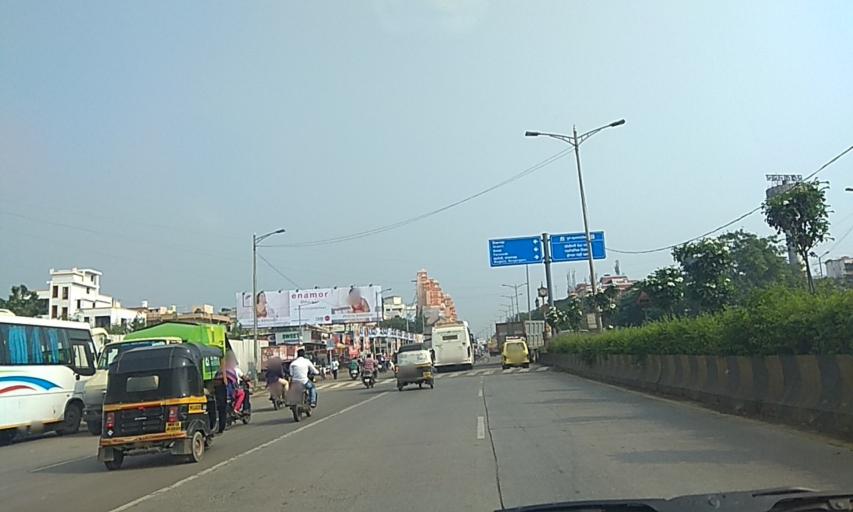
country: IN
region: Maharashtra
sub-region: Pune Division
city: Lohogaon
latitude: 18.5573
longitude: 73.9379
